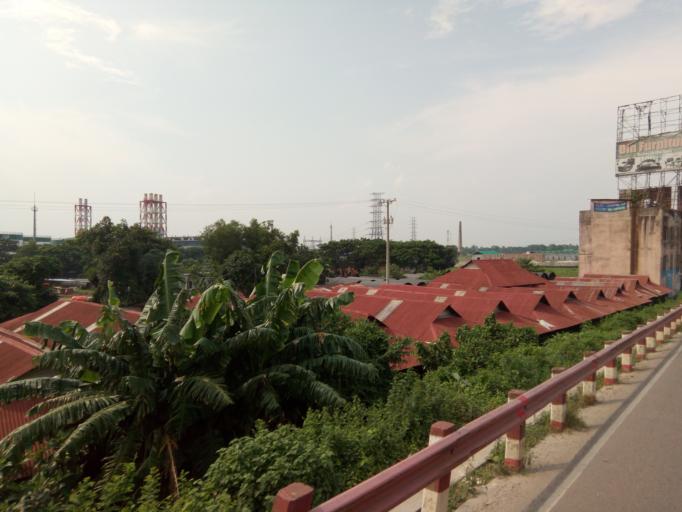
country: BD
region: Dhaka
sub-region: Dhaka
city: Dhaka
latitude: 23.6454
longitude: 90.3490
